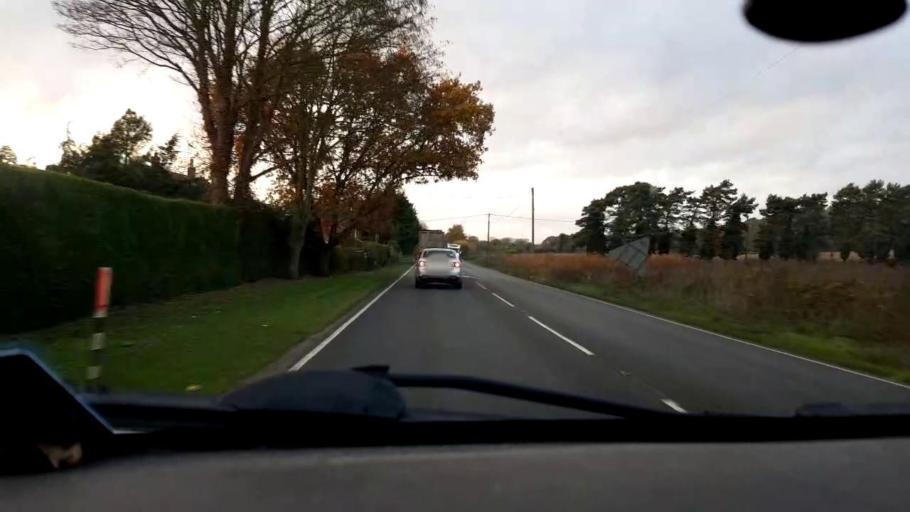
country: GB
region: England
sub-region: Norfolk
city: Costessey
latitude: 52.6967
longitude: 1.1670
